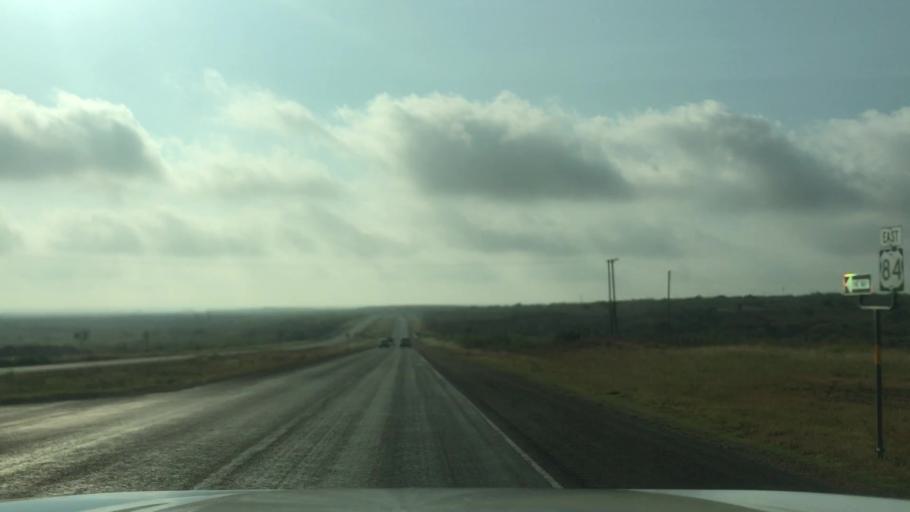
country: US
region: Texas
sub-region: Garza County
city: Post
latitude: 33.1777
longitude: -101.3699
